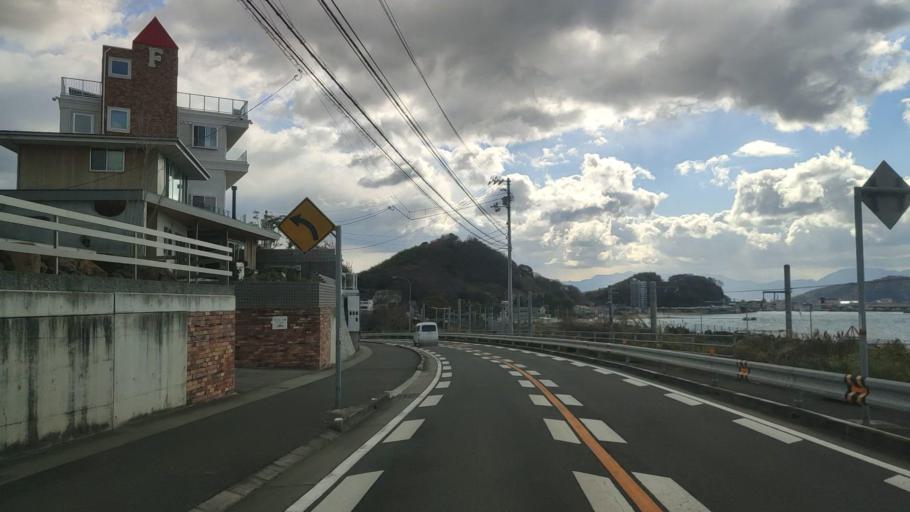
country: JP
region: Ehime
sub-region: Shikoku-chuo Shi
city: Matsuyama
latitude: 33.8773
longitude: 132.7049
